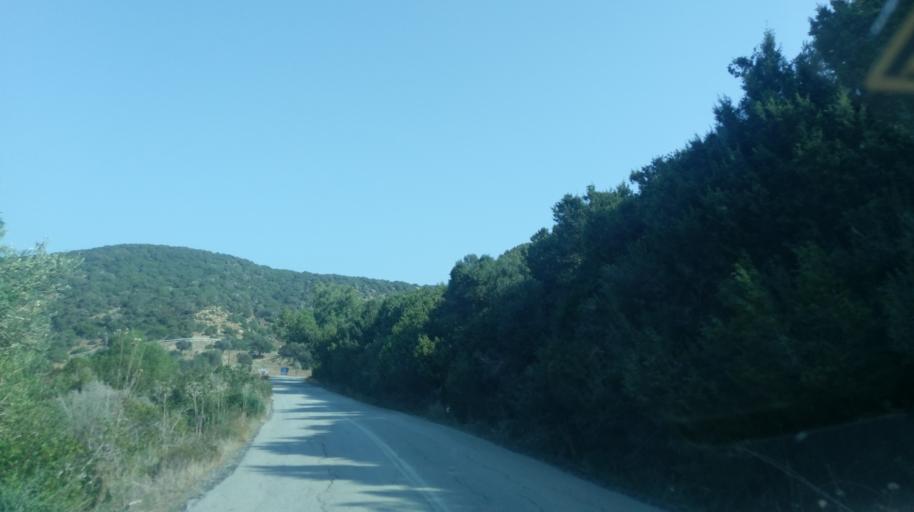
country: CY
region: Ammochostos
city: Rizokarpaso
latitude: 35.6483
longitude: 34.5496
